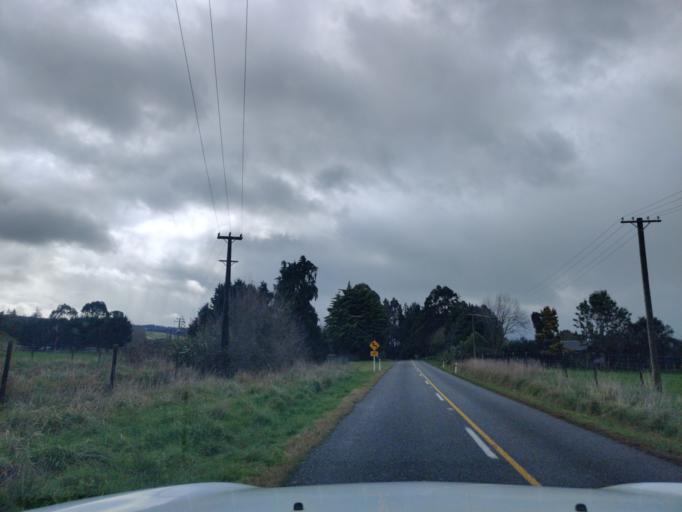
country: NZ
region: Manawatu-Wanganui
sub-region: Palmerston North City
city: Palmerston North
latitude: -40.1836
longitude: 175.7872
